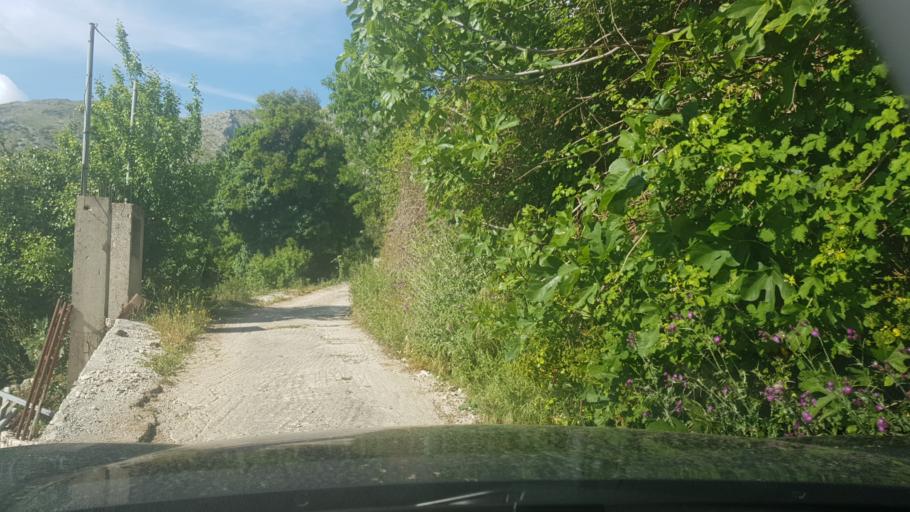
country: GR
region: Ionian Islands
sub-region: Lefkada
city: Nidri
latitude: 38.6888
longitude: 20.6470
